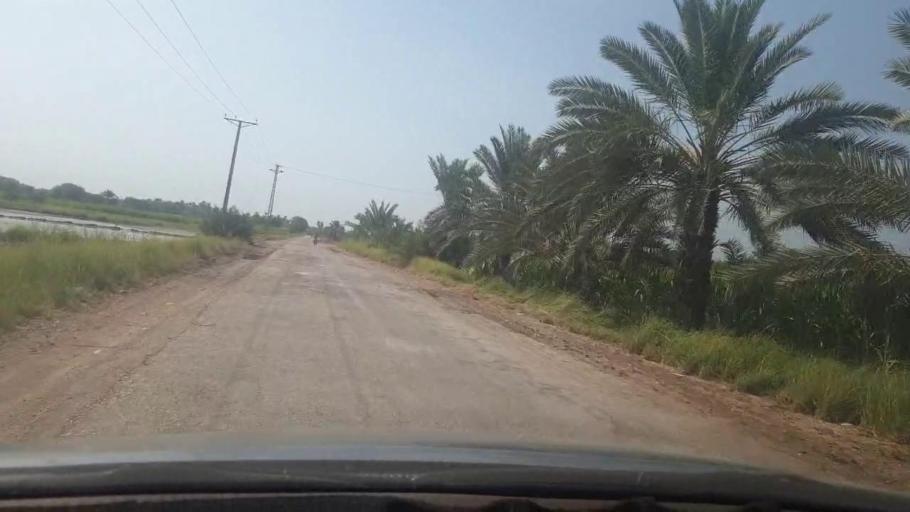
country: PK
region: Sindh
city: Gambat
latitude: 27.3234
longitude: 68.5540
